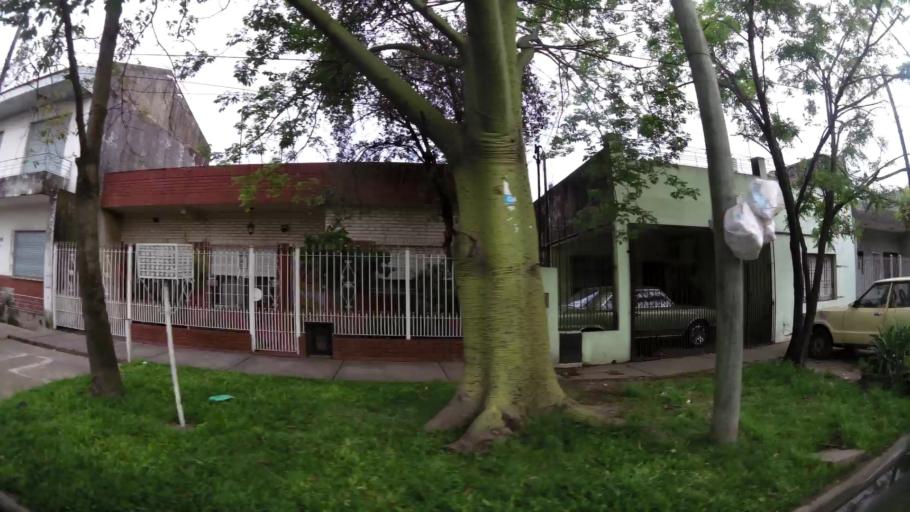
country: AR
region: Buenos Aires
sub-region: Partido de Lanus
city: Lanus
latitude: -34.7238
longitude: -58.3431
